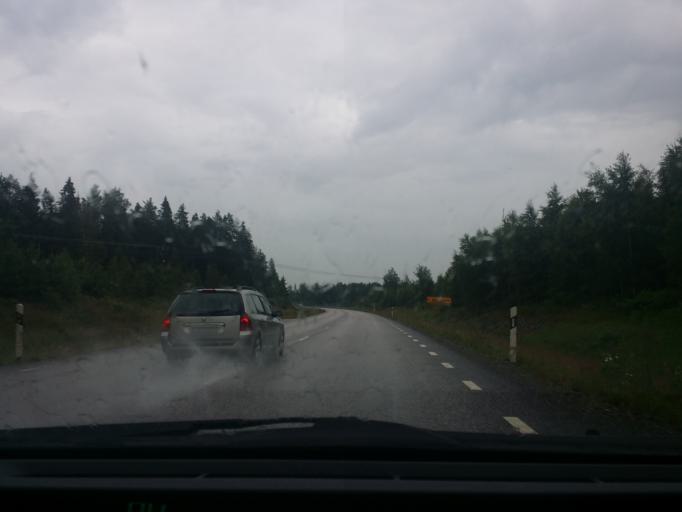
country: SE
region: OErebro
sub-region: Lindesbergs Kommun
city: Frovi
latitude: 59.4606
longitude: 15.4352
